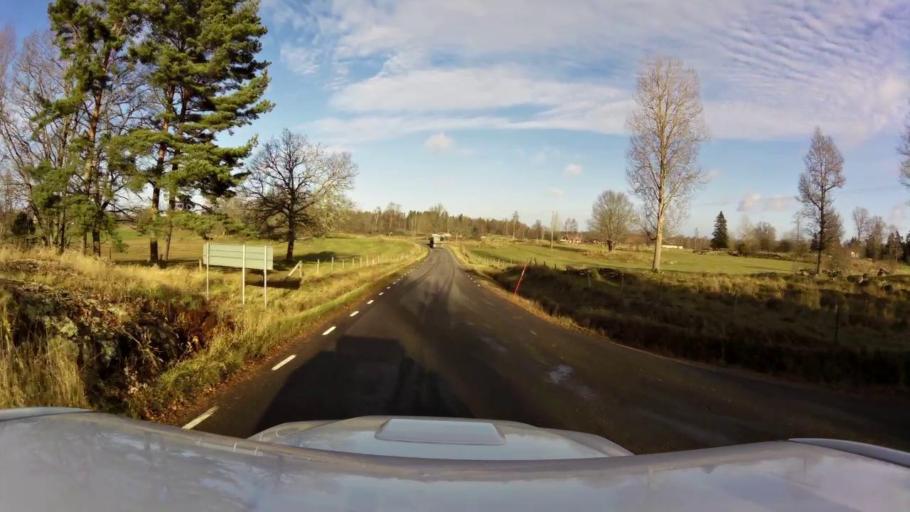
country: SE
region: OEstergoetland
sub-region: Linkopings Kommun
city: Linkoping
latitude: 58.3375
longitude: 15.6525
